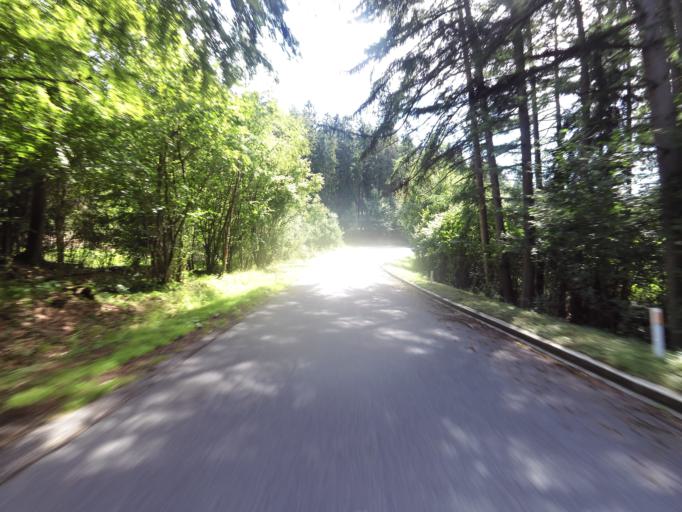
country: BE
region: Wallonia
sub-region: Province du Luxembourg
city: Saint-Hubert
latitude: 50.0414
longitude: 5.3558
